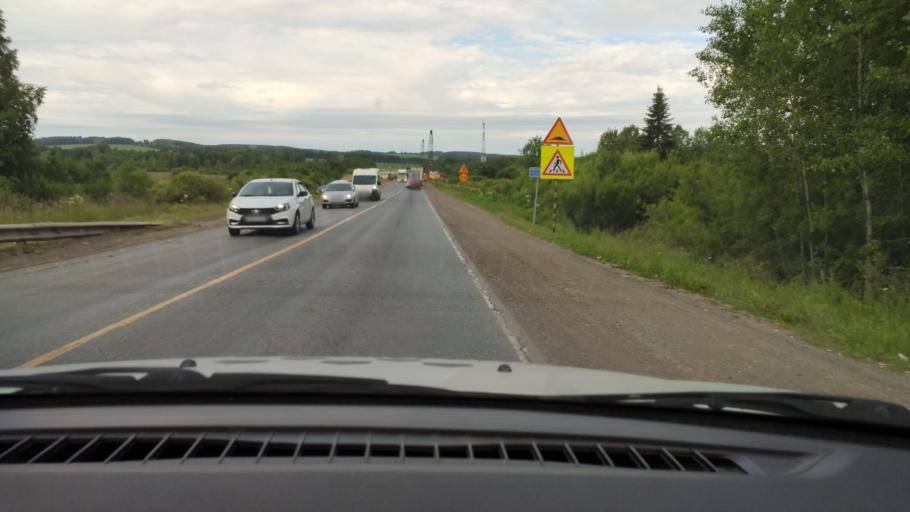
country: RU
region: Perm
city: Nytva
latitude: 57.9815
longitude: 55.2015
